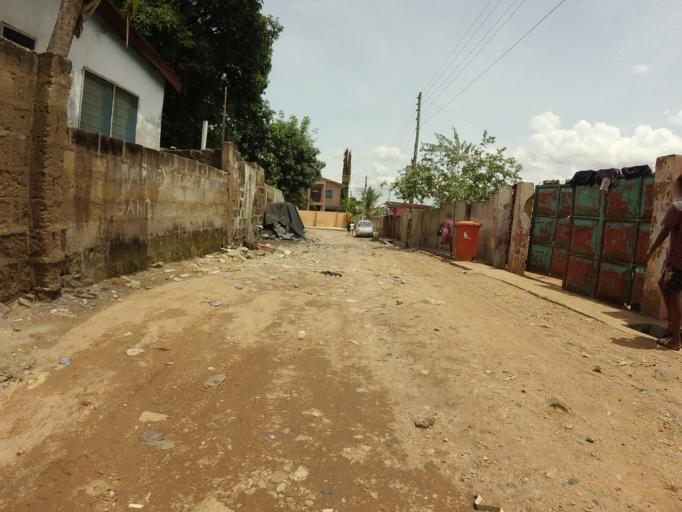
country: GH
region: Greater Accra
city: Dome
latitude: 5.6114
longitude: -0.2428
